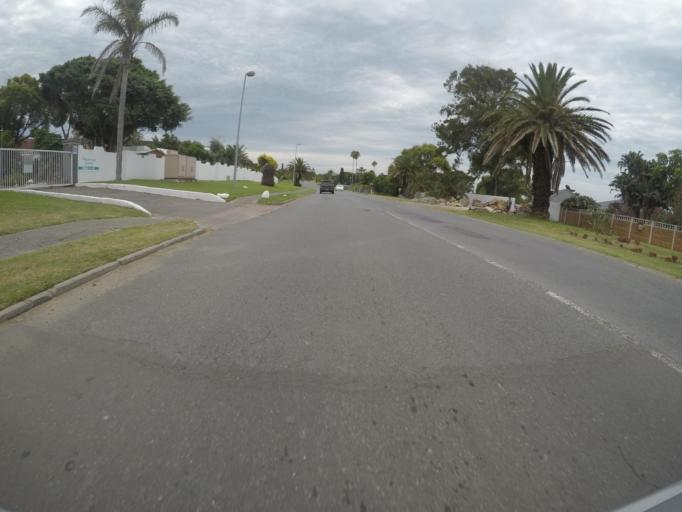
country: ZA
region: Eastern Cape
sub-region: Buffalo City Metropolitan Municipality
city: East London
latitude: -32.9750
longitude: 27.9410
